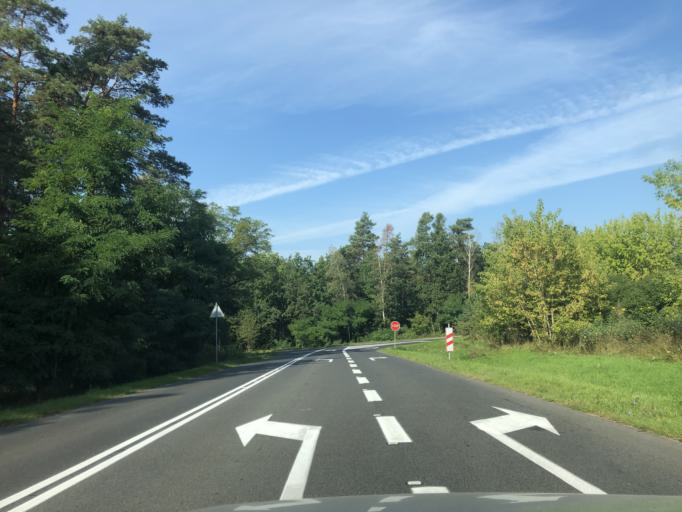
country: PL
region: Greater Poland Voivodeship
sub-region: Powiat pilski
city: Pila
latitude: 53.1318
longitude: 16.8001
